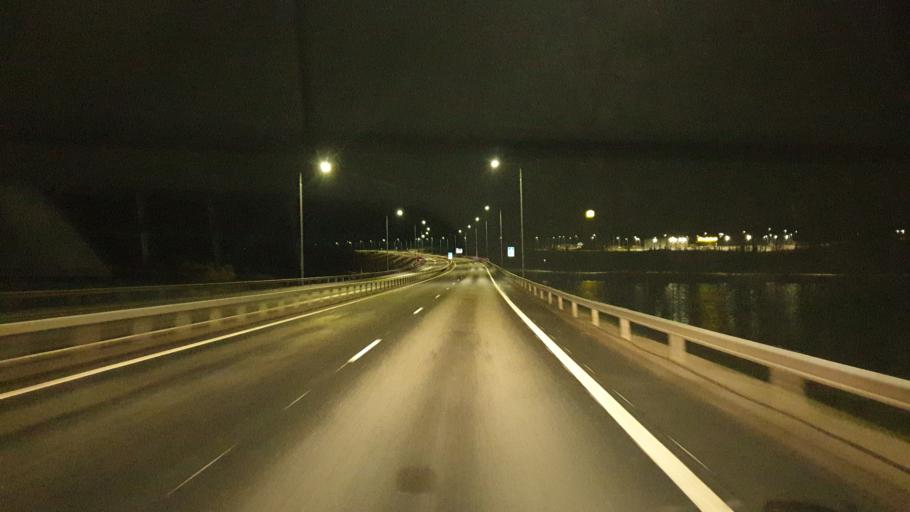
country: FI
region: Central Finland
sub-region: AEaenekoski
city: AEaenekoski
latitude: 62.6024
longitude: 25.6893
